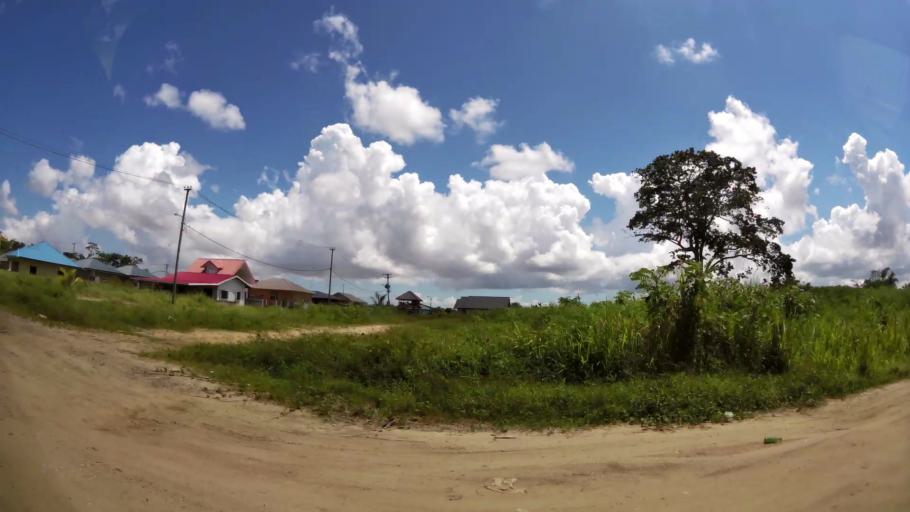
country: SR
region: Paramaribo
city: Paramaribo
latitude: 5.8599
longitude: -55.1493
